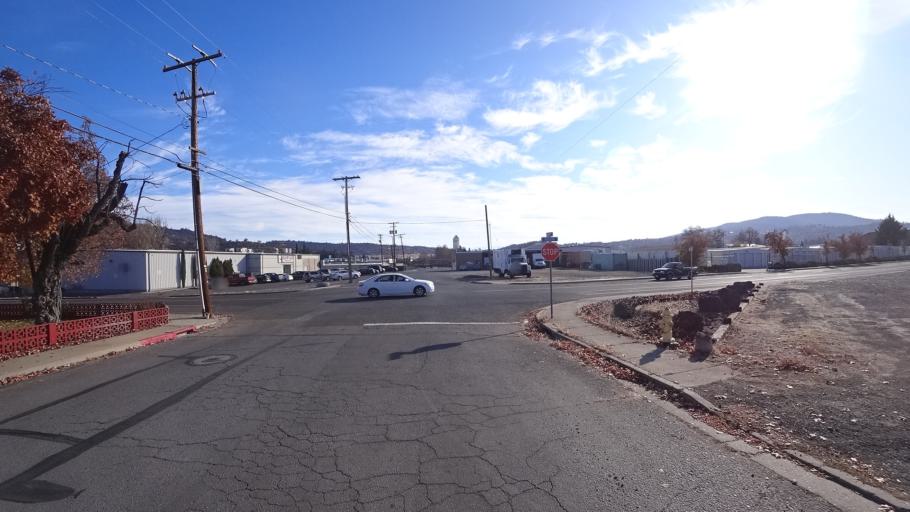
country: US
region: California
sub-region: Siskiyou County
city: Yreka
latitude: 41.7158
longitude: -122.6430
